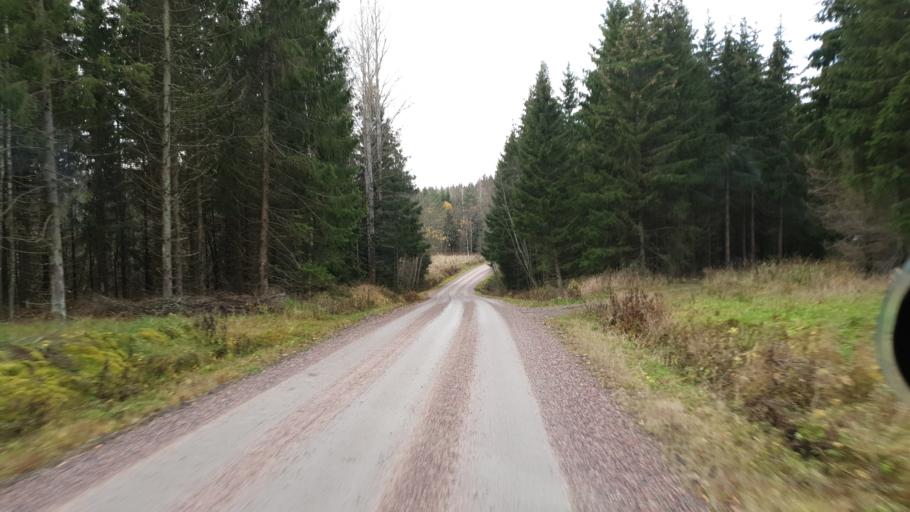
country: FI
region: Uusimaa
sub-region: Helsinki
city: Siuntio
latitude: 60.1475
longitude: 24.2714
